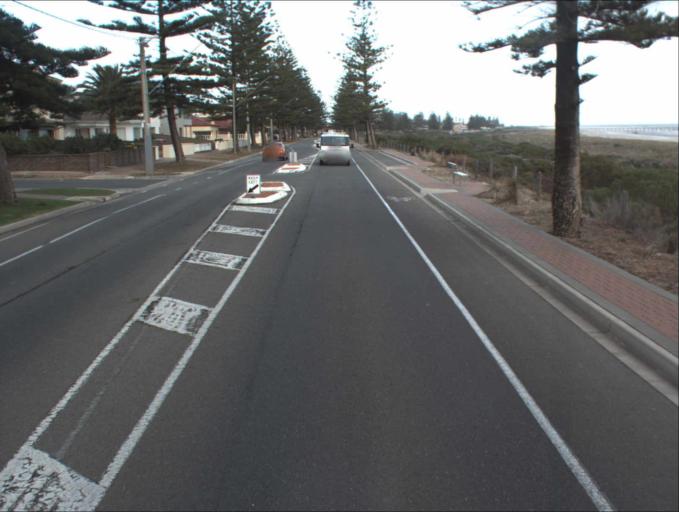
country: AU
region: South Australia
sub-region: Port Adelaide Enfield
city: Birkenhead
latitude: -34.8133
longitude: 138.4911
